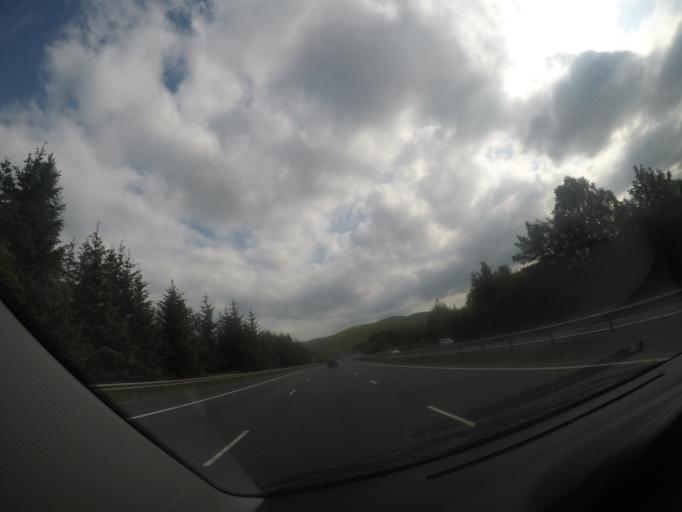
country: GB
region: Scotland
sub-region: South Lanarkshire
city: Douglas
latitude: 55.4871
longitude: -3.6950
